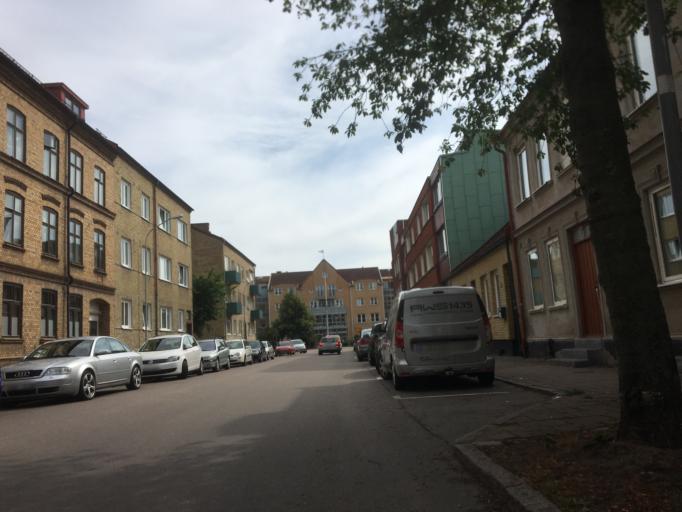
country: SE
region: Skane
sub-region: Landskrona
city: Landskrona
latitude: 55.8772
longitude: 12.8301
